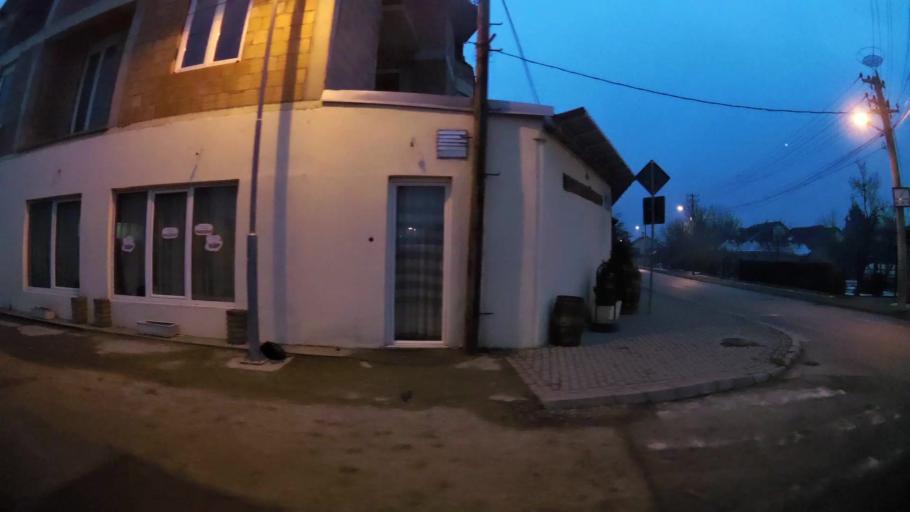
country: MK
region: Kisela Voda
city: Kisela Voda
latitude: 41.9691
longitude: 21.4873
